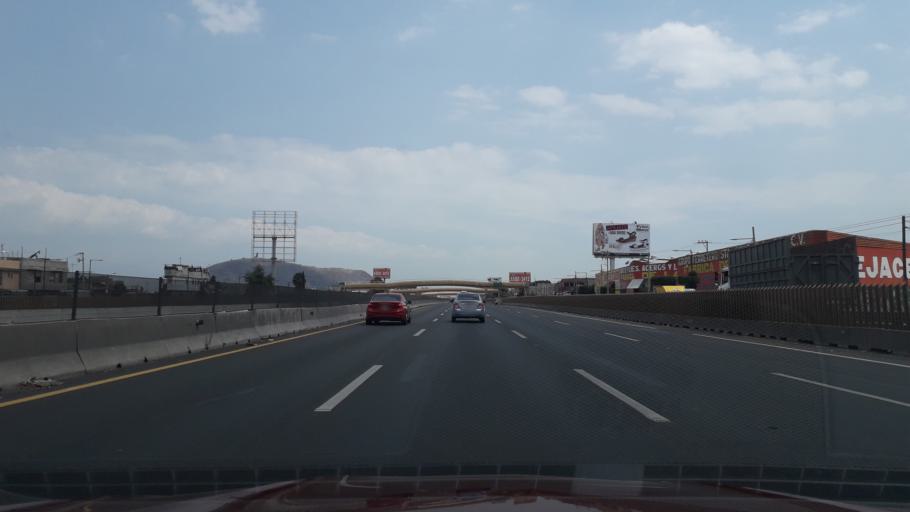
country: MX
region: Mexico
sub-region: La Paz
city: San Isidro
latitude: 19.3131
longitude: -98.9461
